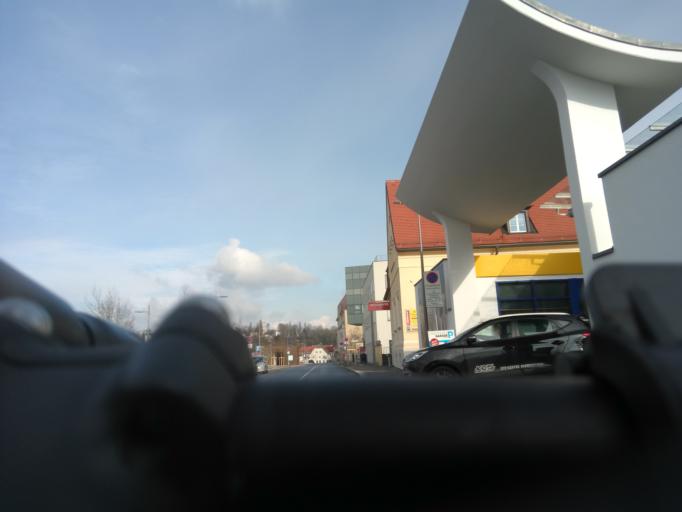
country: AT
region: Upper Austria
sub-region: Steyr Stadt
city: Steyr
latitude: 48.0375
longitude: 14.4210
